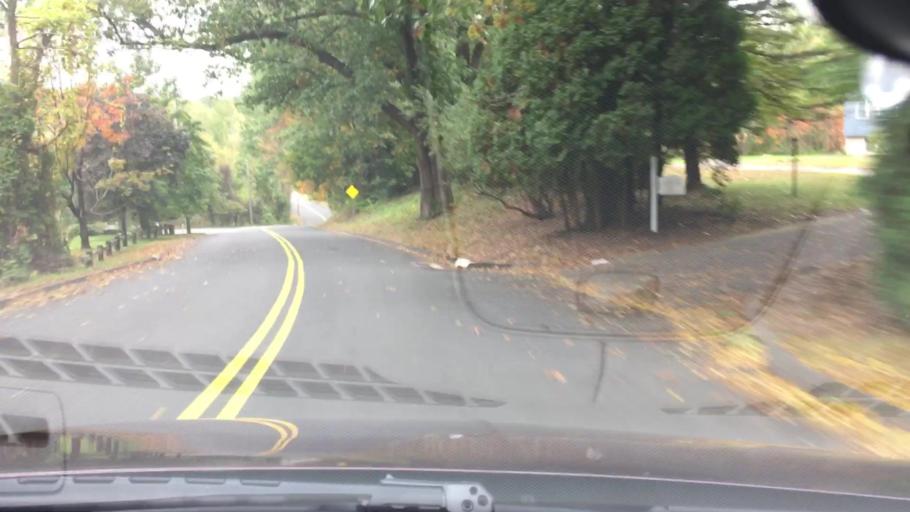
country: US
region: Connecticut
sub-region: Hartford County
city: Broad Brook
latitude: 41.9161
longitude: -72.5533
